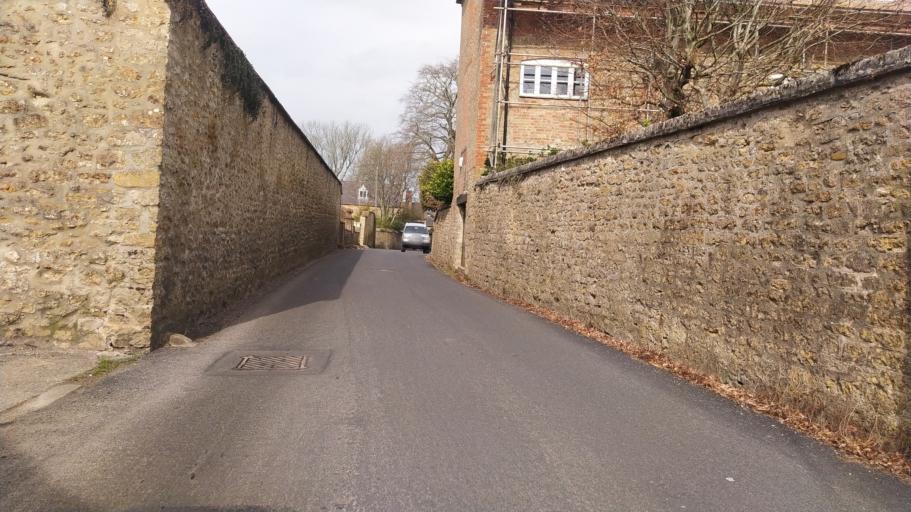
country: GB
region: England
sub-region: Dorset
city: Beaminster
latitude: 50.8068
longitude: -2.7350
